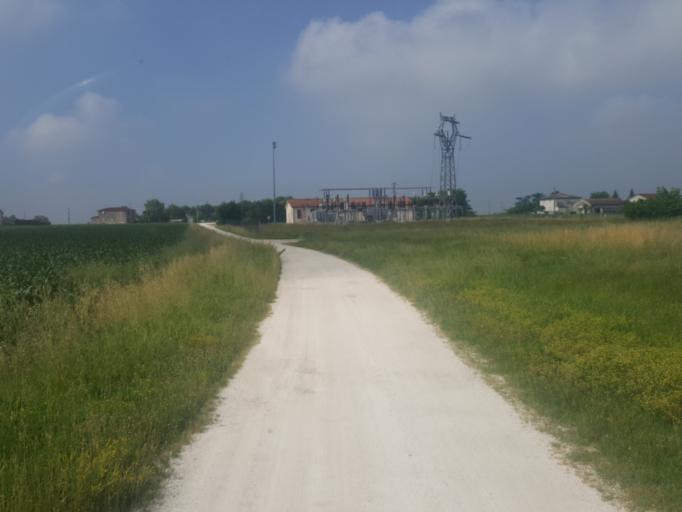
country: IT
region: Veneto
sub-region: Provincia di Rovigo
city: Canaro
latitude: 44.9404
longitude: 11.6501
